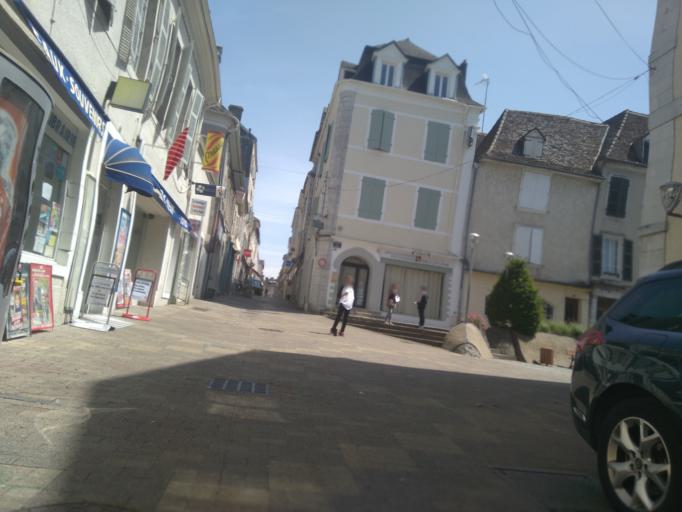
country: FR
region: Aquitaine
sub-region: Departement des Pyrenees-Atlantiques
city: Orthez
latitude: 43.4901
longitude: -0.7749
